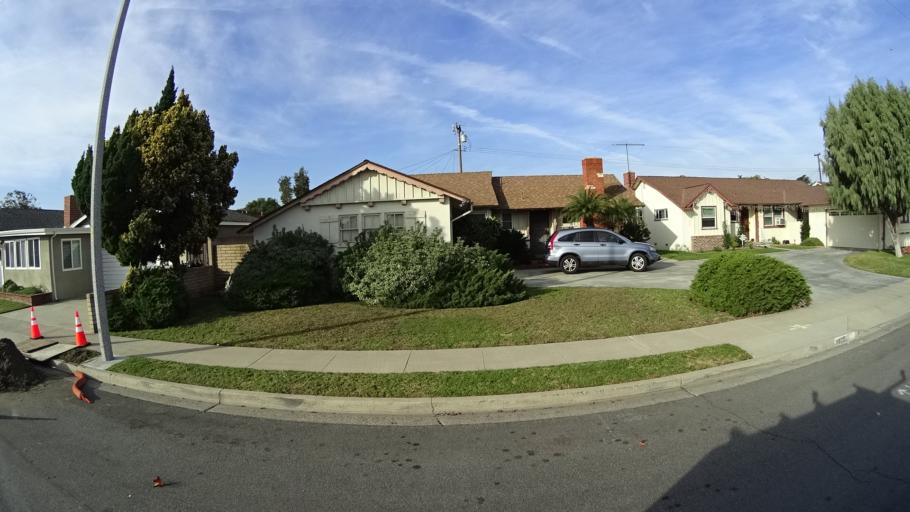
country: US
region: California
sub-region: Orange County
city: Garden Grove
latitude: 33.7941
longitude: -117.9305
